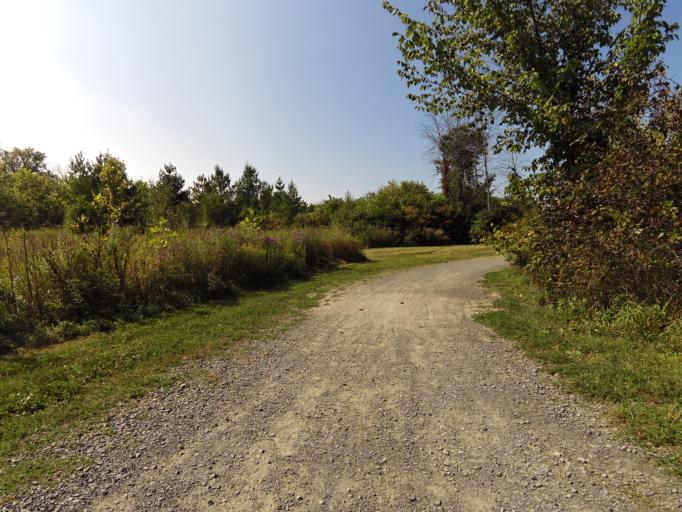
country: CA
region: Ontario
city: Bells Corners
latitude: 45.2621
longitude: -75.7308
